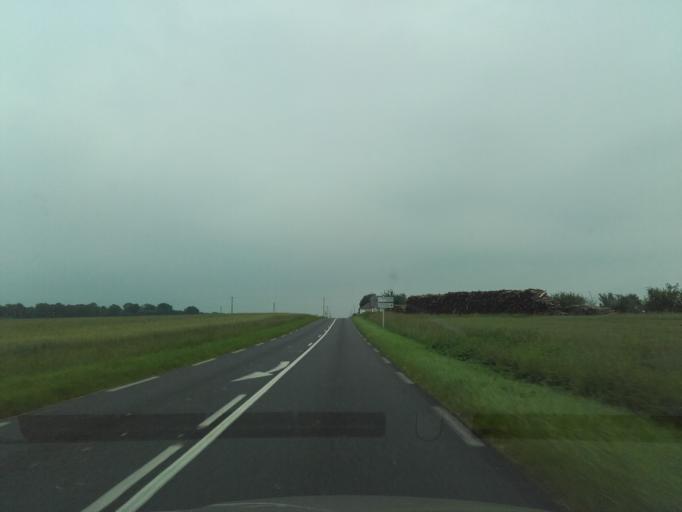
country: FR
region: Centre
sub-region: Departement d'Indre-et-Loire
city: Cerelles
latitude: 47.5186
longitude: 0.6947
